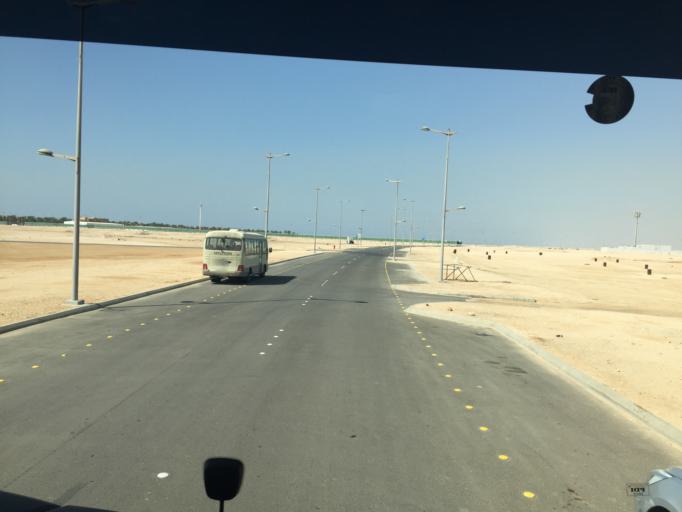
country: SA
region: Makkah
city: Rabigh
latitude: 22.4083
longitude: 39.0829
